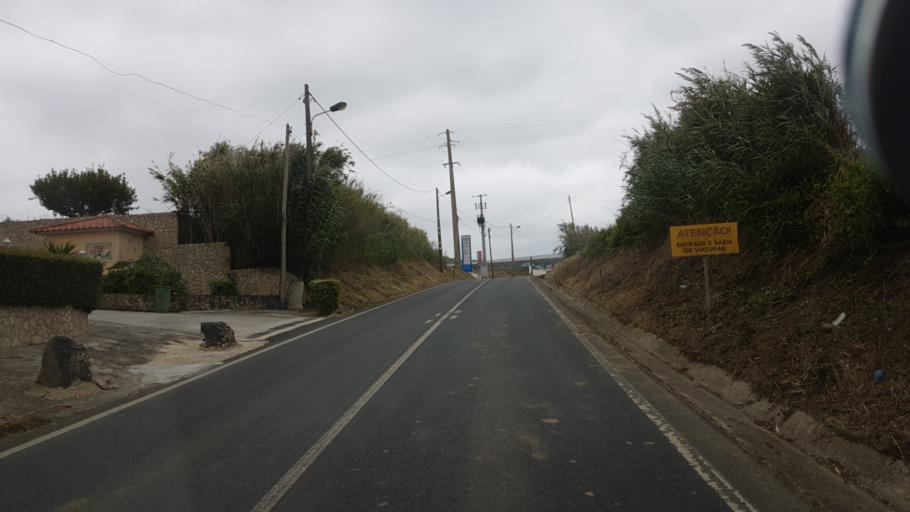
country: PT
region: Lisbon
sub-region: Lourinha
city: Lourinha
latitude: 39.2303
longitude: -9.3121
